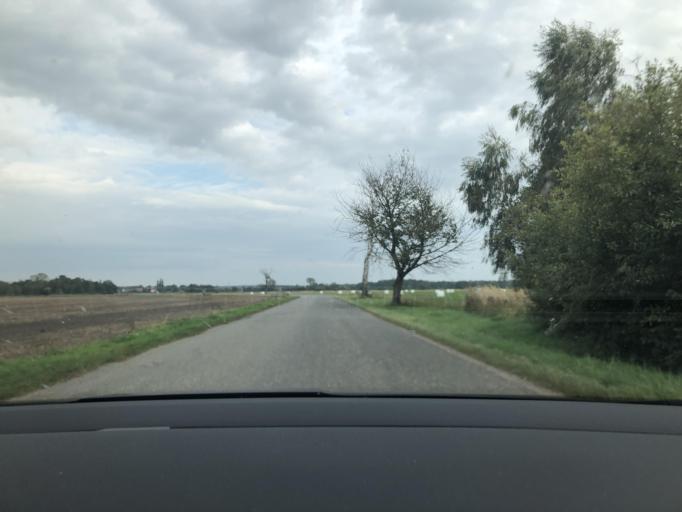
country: CZ
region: Pardubicky
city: Recany nad Labem
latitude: 50.0793
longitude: 15.4546
